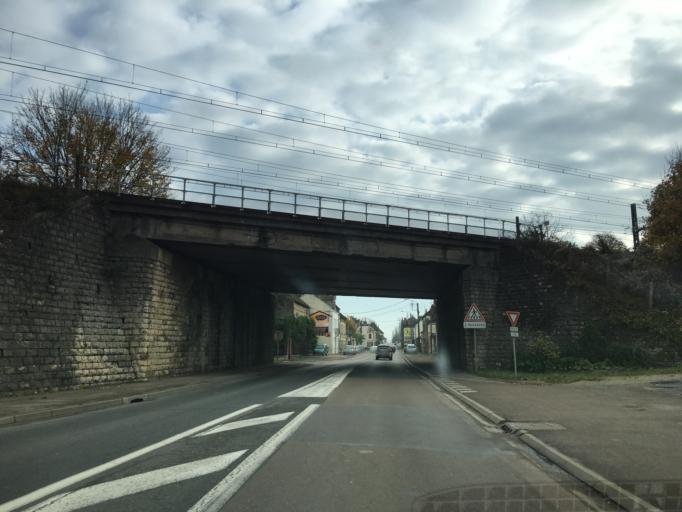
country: FR
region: Bourgogne
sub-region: Departement de l'Yonne
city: Pont-sur-Yonne
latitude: 48.2906
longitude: 3.2010
